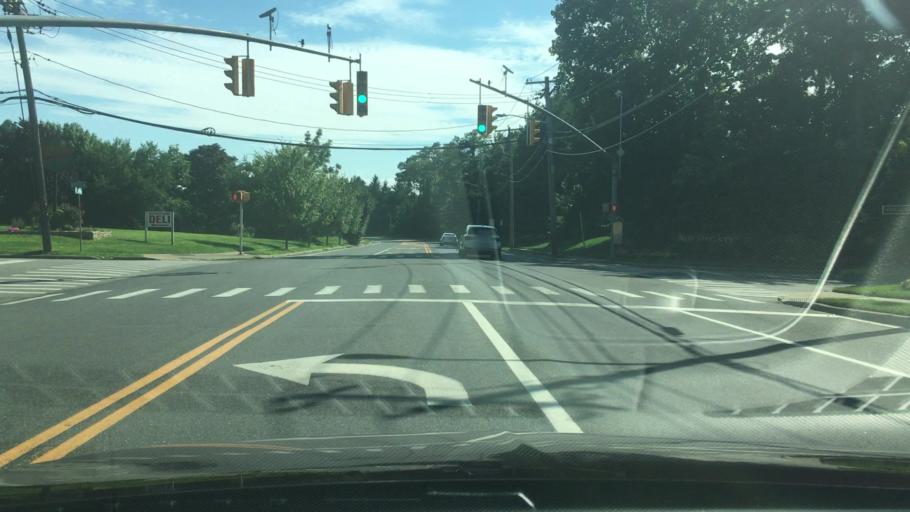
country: US
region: New York
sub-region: Suffolk County
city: Melville
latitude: 40.7742
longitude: -73.4268
